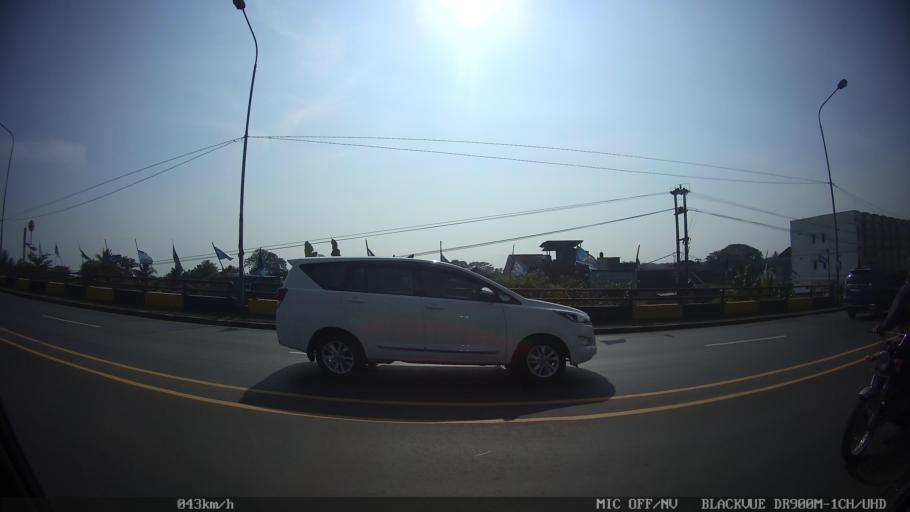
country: ID
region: Lampung
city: Natar
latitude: -5.3215
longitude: 105.2001
